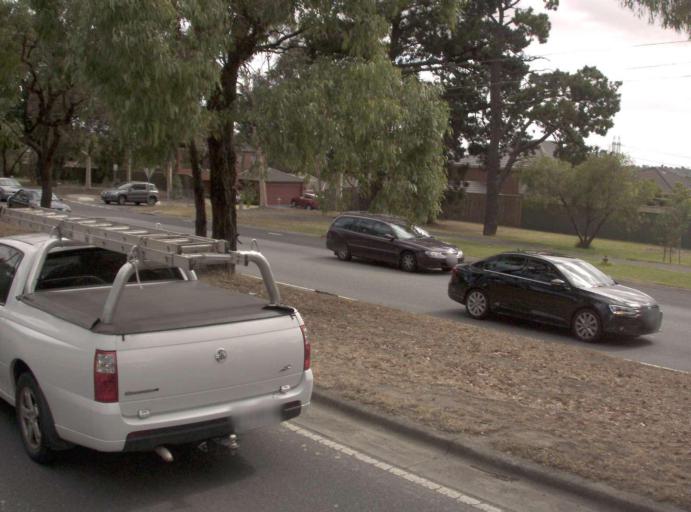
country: AU
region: Victoria
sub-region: Knox
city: Rowville
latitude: -37.9241
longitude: 145.2339
